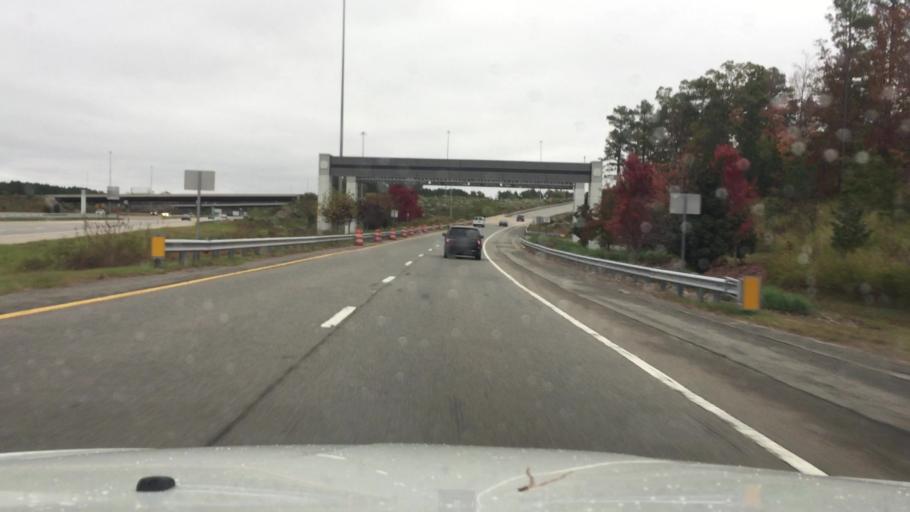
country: US
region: North Carolina
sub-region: Wake County
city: Morrisville
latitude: 35.8498
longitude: -78.8642
